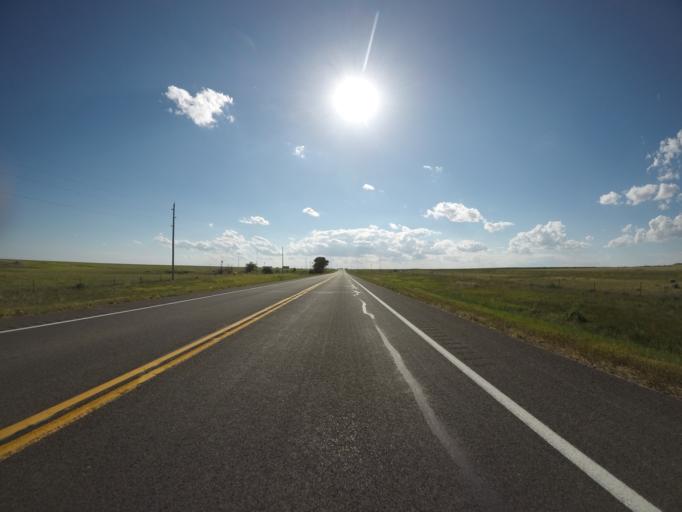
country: US
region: Colorado
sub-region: Morgan County
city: Fort Morgan
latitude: 40.6113
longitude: -103.8172
